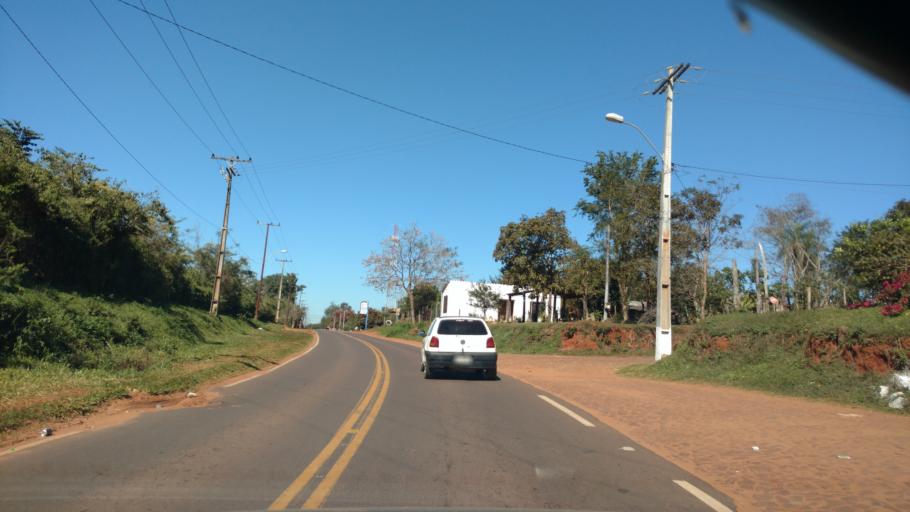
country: PY
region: Paraguari
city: Yaguaron
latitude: -25.5523
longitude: -57.2831
